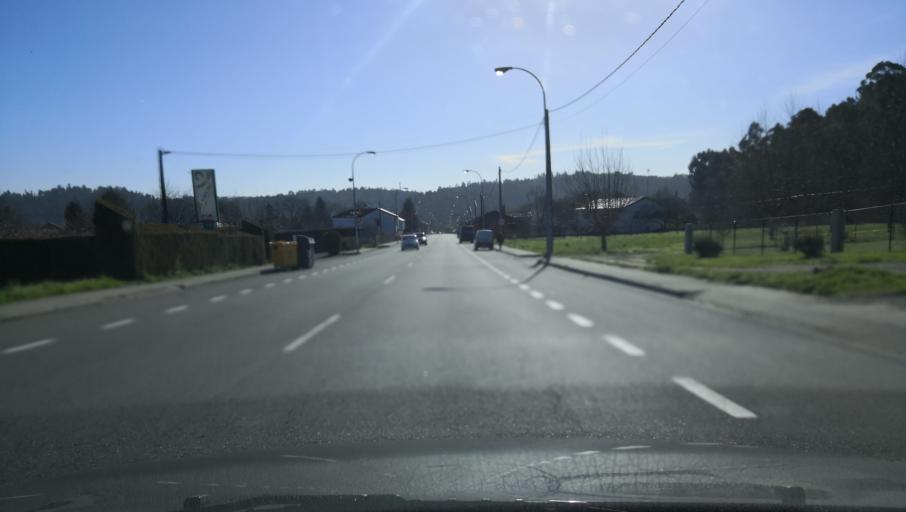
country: ES
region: Galicia
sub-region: Provincia de Pontevedra
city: Silleda
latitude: 42.7384
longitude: -8.3265
